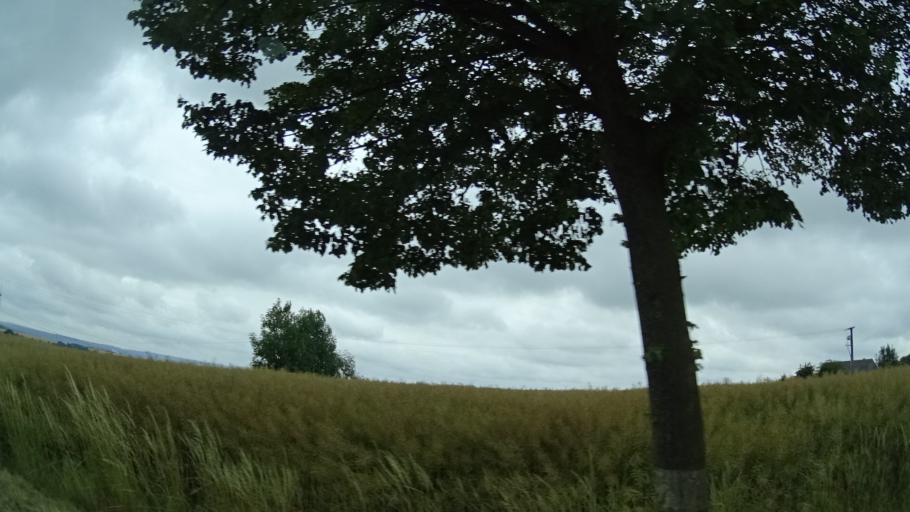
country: LU
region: Luxembourg
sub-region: Canton de Capellen
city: Dippach
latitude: 49.5823
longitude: 5.9794
